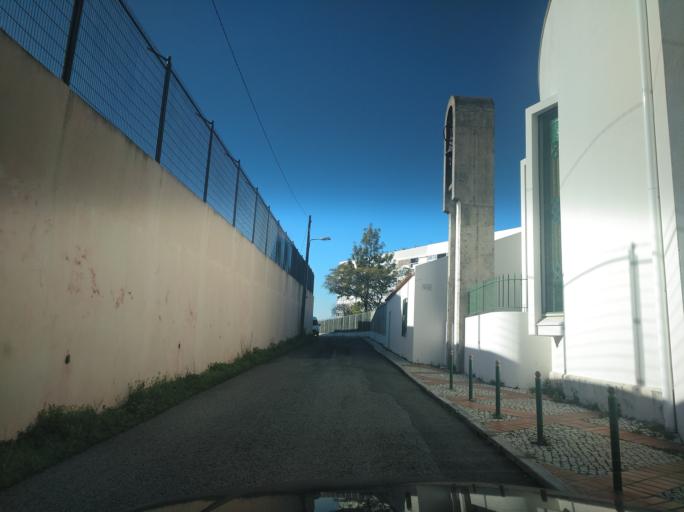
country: PT
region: Lisbon
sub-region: Loures
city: Moscavide
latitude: 38.7803
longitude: -9.1138
